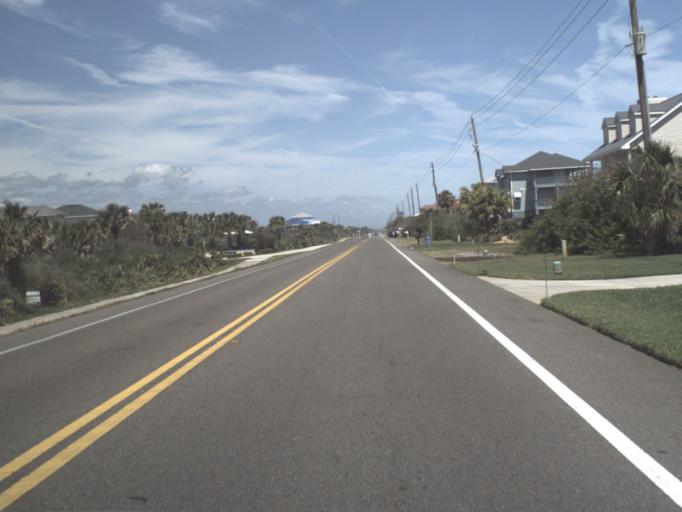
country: US
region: Florida
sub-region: Flagler County
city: Flagler Beach
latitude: 29.5299
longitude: -81.1520
